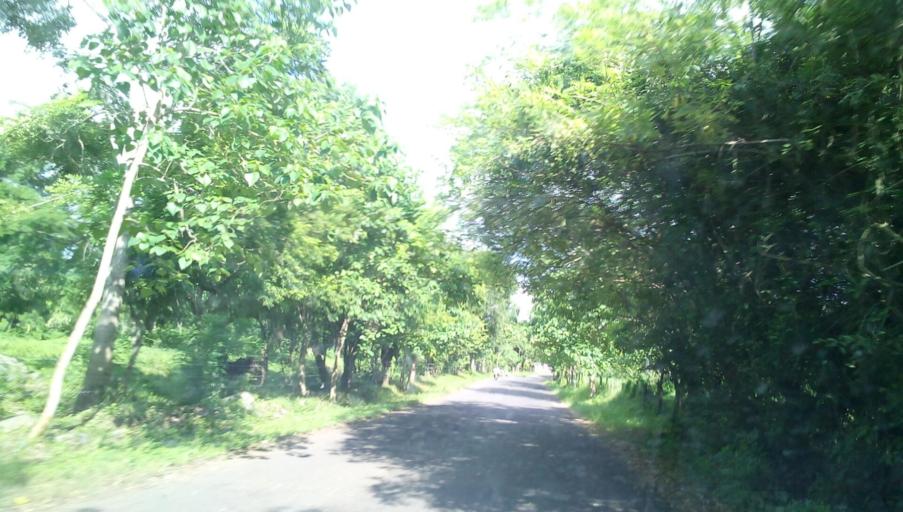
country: MX
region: Veracruz
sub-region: Citlaltepetl
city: Las Sabinas
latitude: 21.3551
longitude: -97.8984
